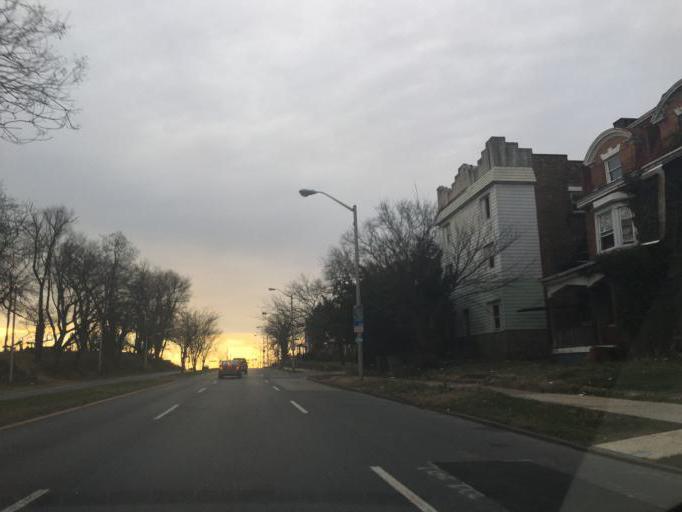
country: US
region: Maryland
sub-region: City of Baltimore
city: Baltimore
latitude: 39.3206
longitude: -76.6542
